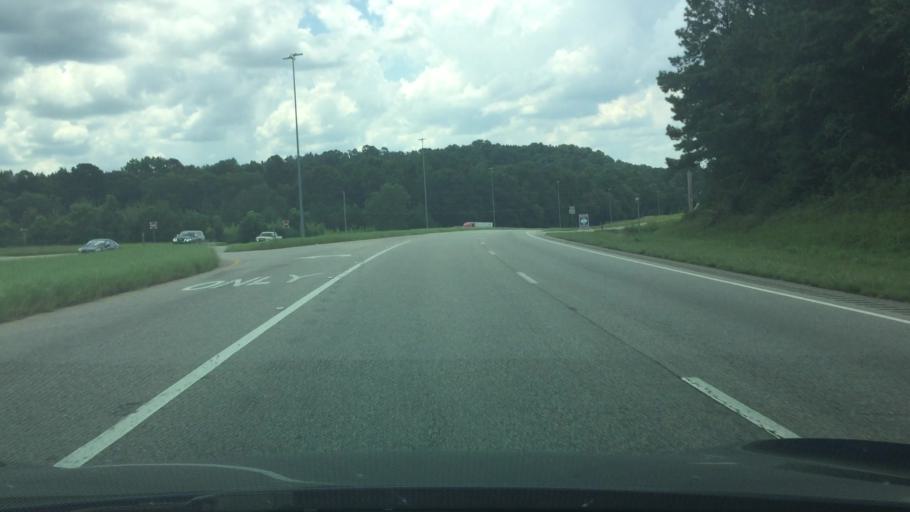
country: US
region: Alabama
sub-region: Pike County
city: Troy
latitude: 31.8332
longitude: -85.9911
